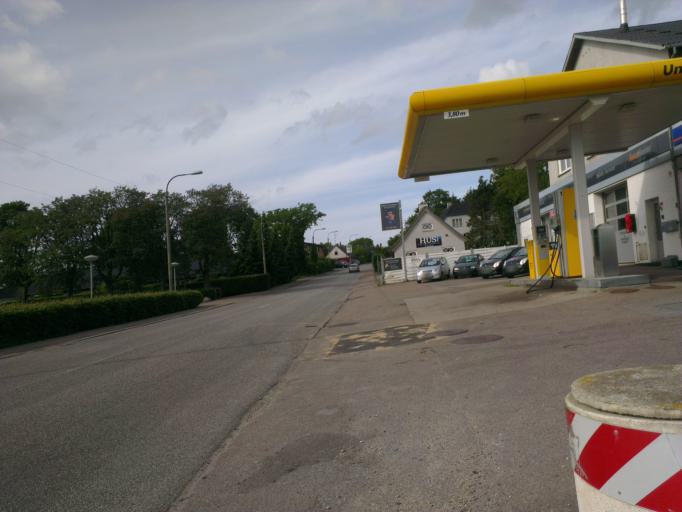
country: DK
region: Capital Region
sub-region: Frederikssund Kommune
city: Skibby
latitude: 55.7450
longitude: 11.9543
